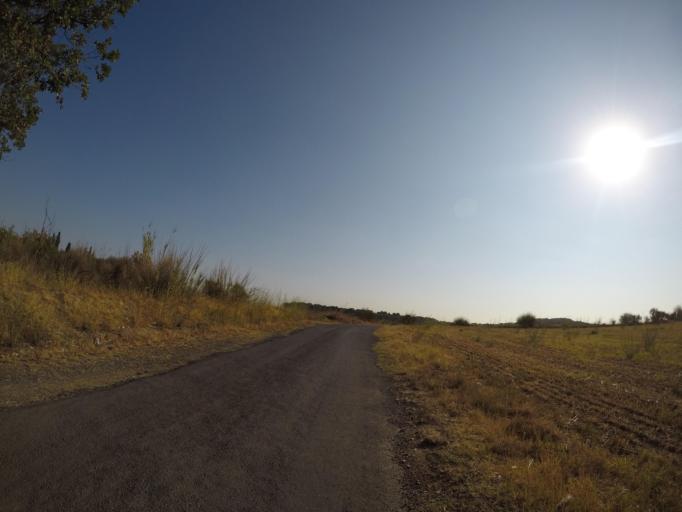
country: FR
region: Languedoc-Roussillon
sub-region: Departement des Pyrenees-Orientales
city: Pollestres
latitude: 42.6694
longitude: 2.8639
